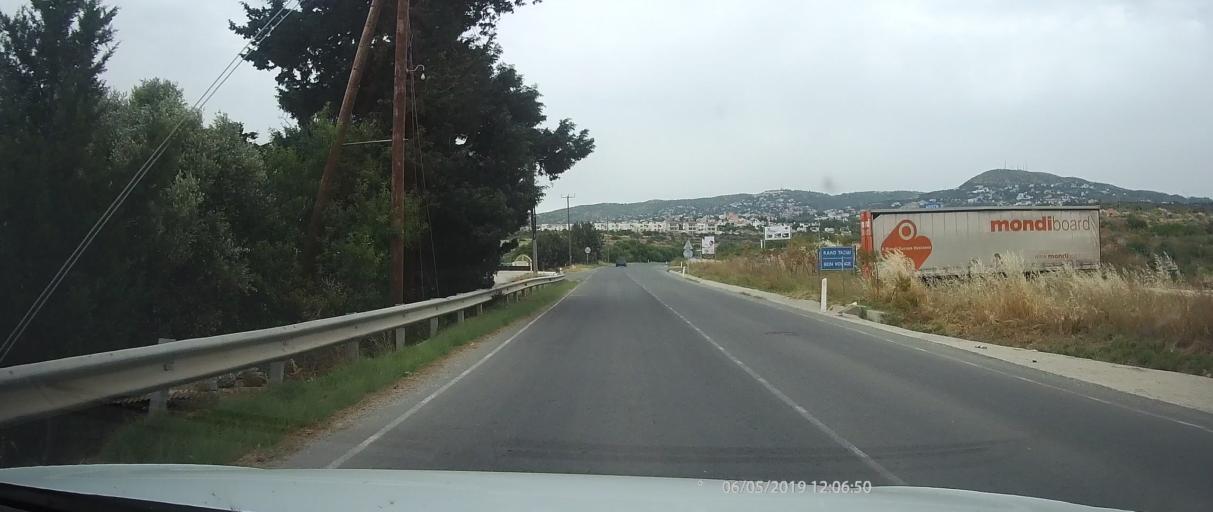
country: CY
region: Pafos
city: Empa
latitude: 34.8214
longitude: 32.4230
